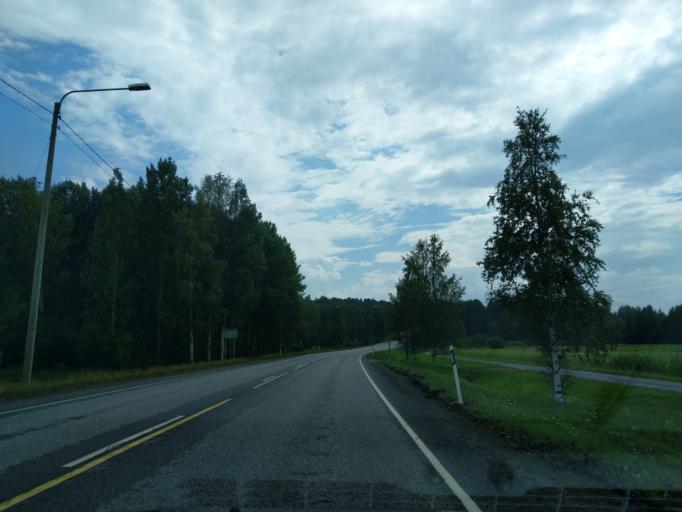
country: FI
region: South Karelia
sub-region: Imatra
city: Parikkala
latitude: 61.5745
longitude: 29.5045
